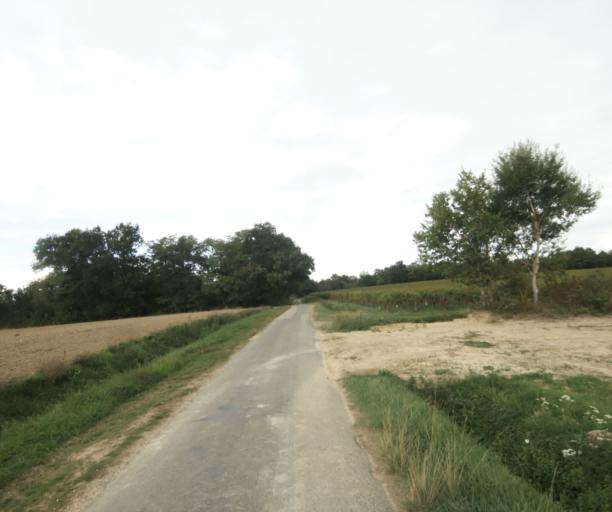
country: FR
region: Midi-Pyrenees
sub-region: Departement du Gers
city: Eauze
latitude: 43.8917
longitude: 0.1083
